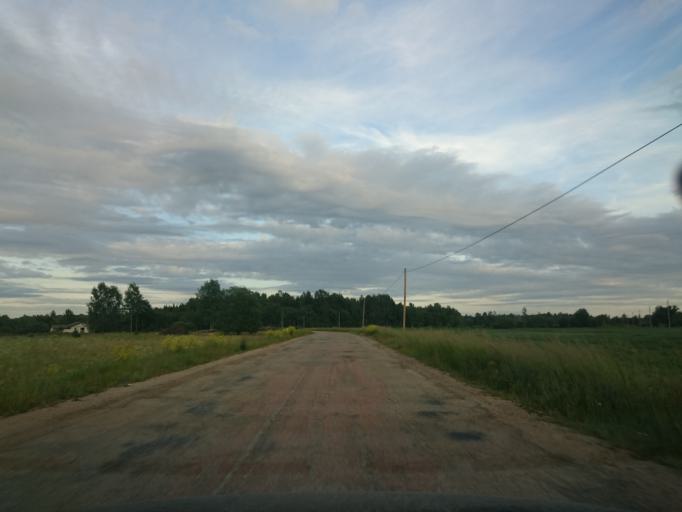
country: LV
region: Ropazu
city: Ropazi
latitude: 56.9595
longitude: 24.6927
